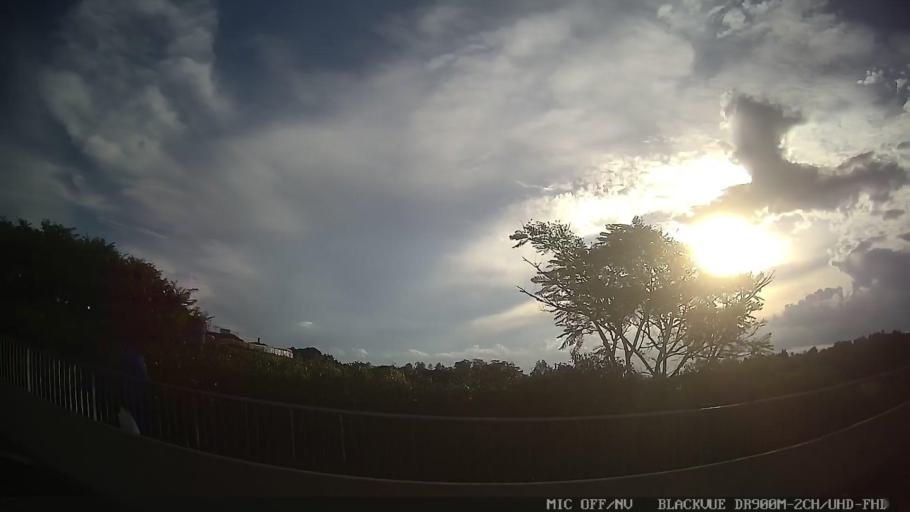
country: BR
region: Sao Paulo
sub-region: Tiete
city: Tiete
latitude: -23.1143
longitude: -47.7196
